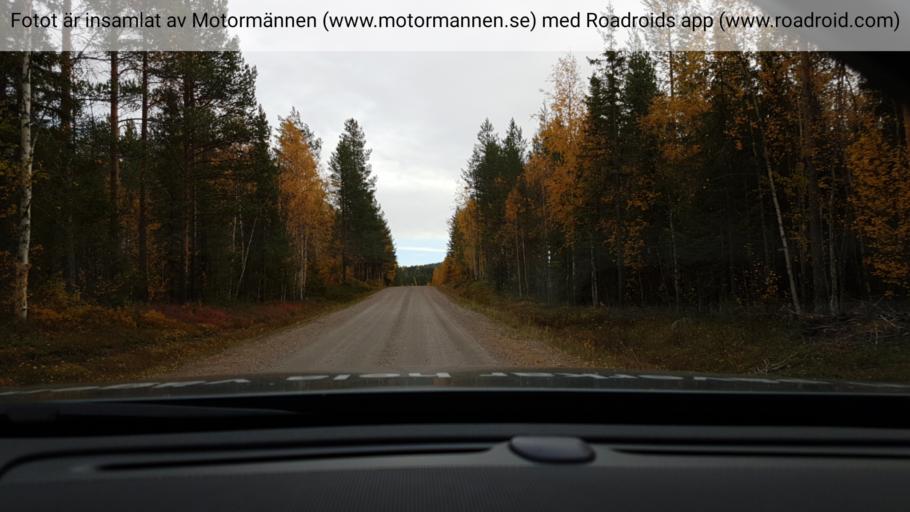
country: SE
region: Norrbotten
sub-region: Overkalix Kommun
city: OEverkalix
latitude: 66.2906
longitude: 22.9586
